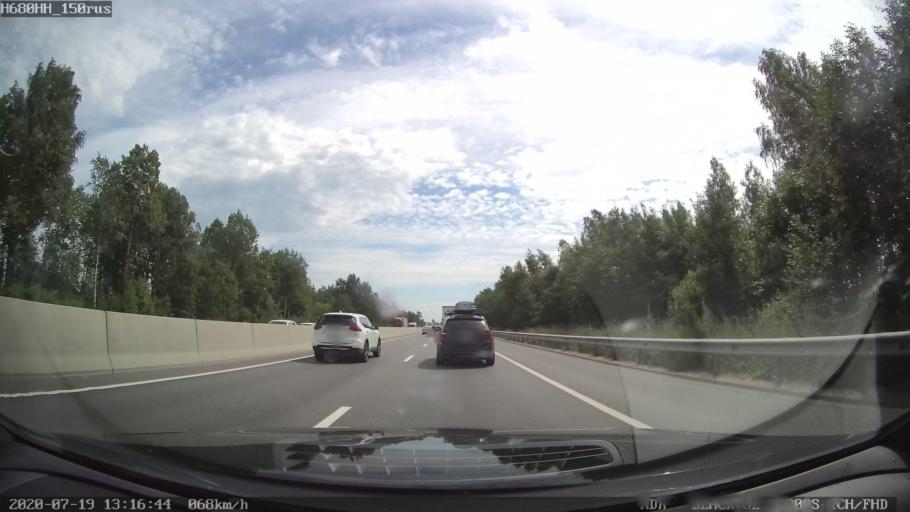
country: RU
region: St.-Petersburg
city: Kolpino
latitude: 59.7148
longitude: 30.5590
